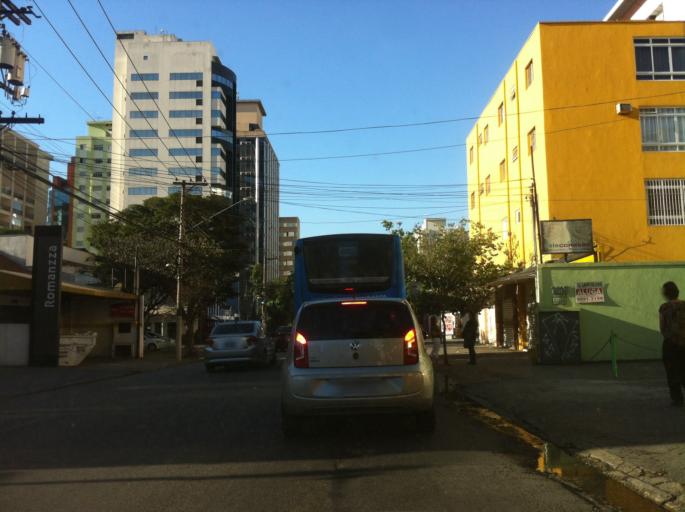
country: BR
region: Sao Paulo
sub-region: Sao Paulo
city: Sao Paulo
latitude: -23.6119
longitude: -46.6640
